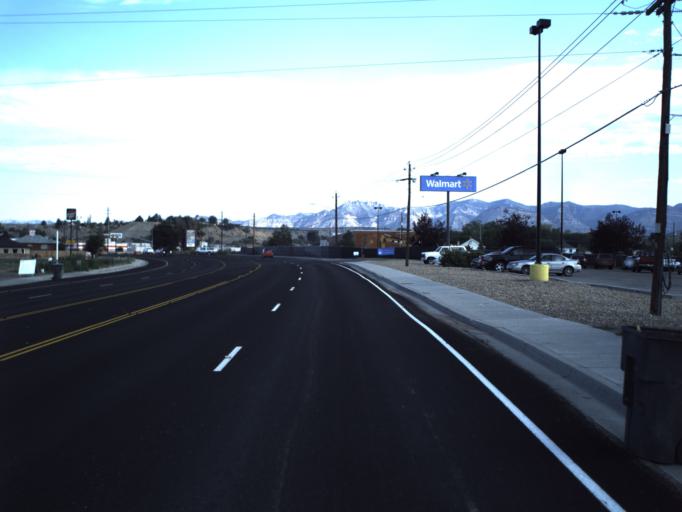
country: US
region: Utah
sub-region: Carbon County
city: Price
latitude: 39.5952
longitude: -110.7907
